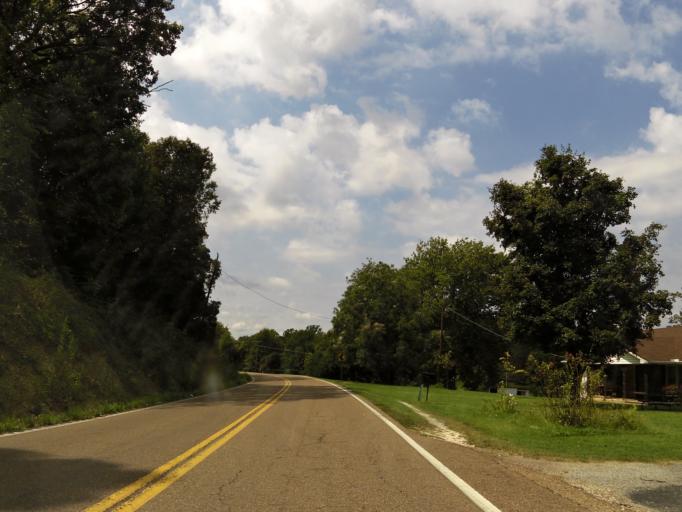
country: US
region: Tennessee
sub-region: Decatur County
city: Decaturville
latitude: 35.6005
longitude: -88.0491
